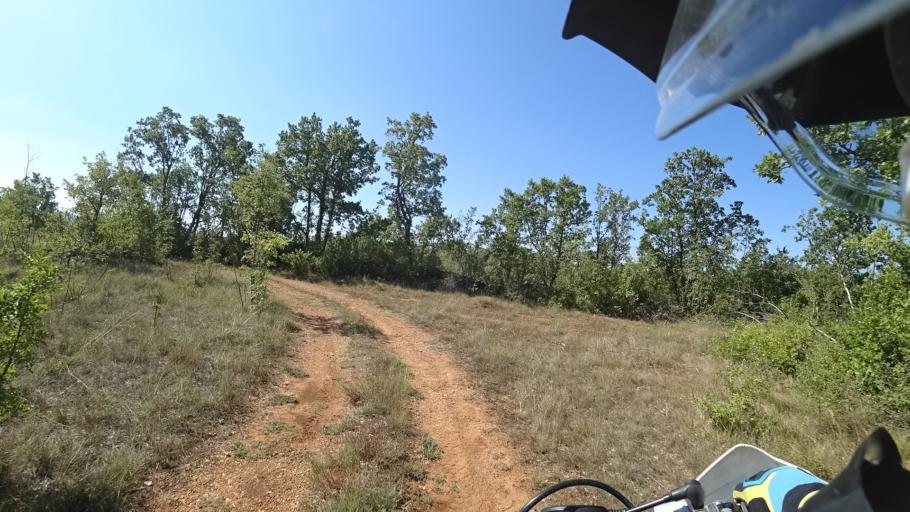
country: HR
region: Sibensko-Kniniska
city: Drnis
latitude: 43.8496
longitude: 16.2757
